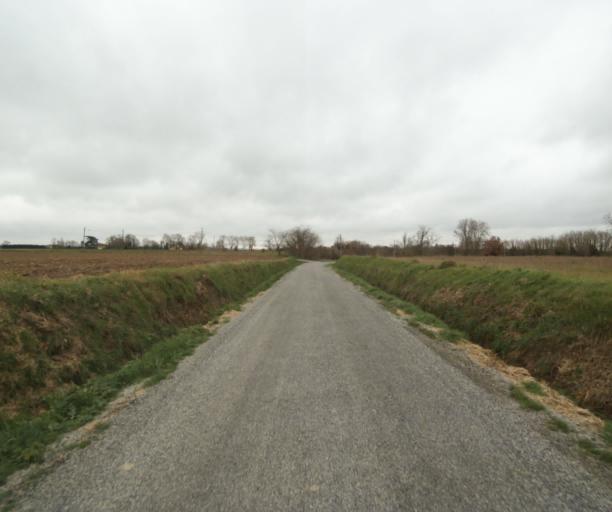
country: FR
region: Midi-Pyrenees
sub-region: Departement de l'Ariege
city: Mazeres
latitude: 43.2369
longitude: 1.6811
